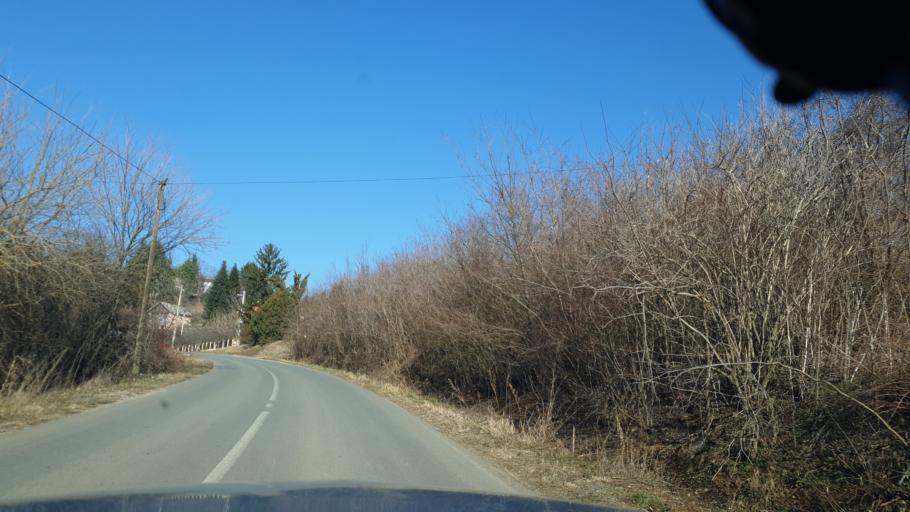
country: RS
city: Vrdnik
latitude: 45.1152
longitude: 19.7737
